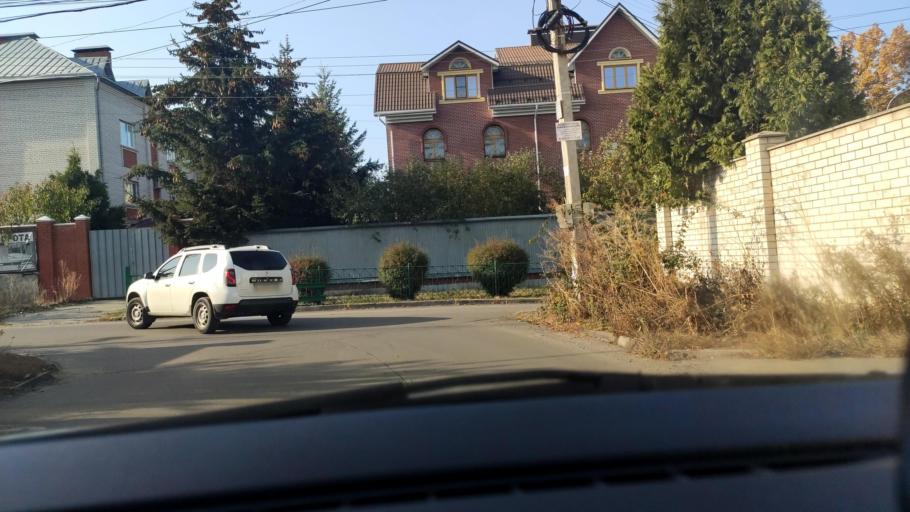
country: RU
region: Voronezj
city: Voronezh
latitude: 51.7078
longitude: 39.1992
